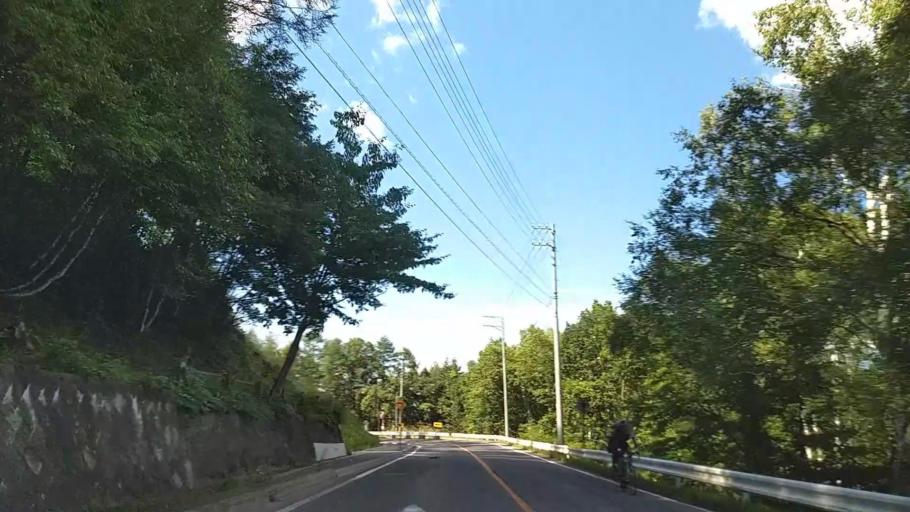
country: JP
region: Nagano
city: Chino
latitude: 36.1113
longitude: 138.2532
